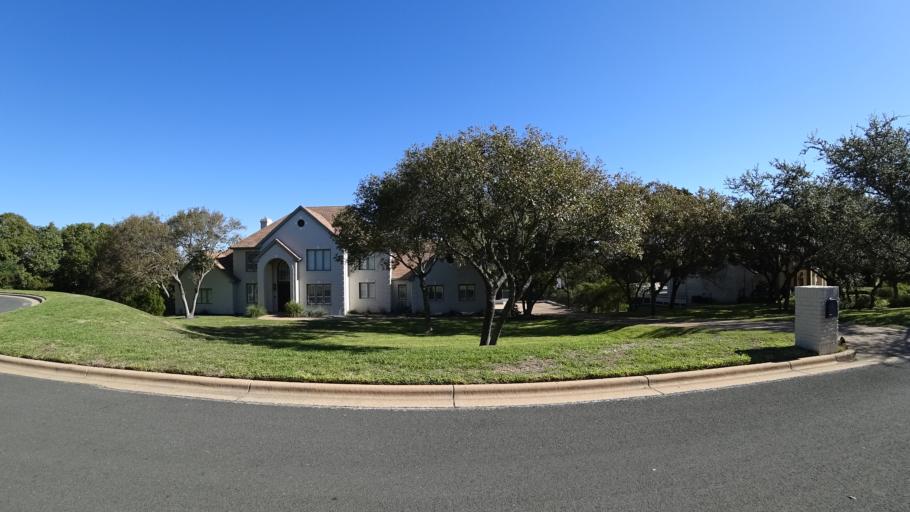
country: US
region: Texas
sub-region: Travis County
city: West Lake Hills
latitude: 30.3318
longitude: -97.7940
